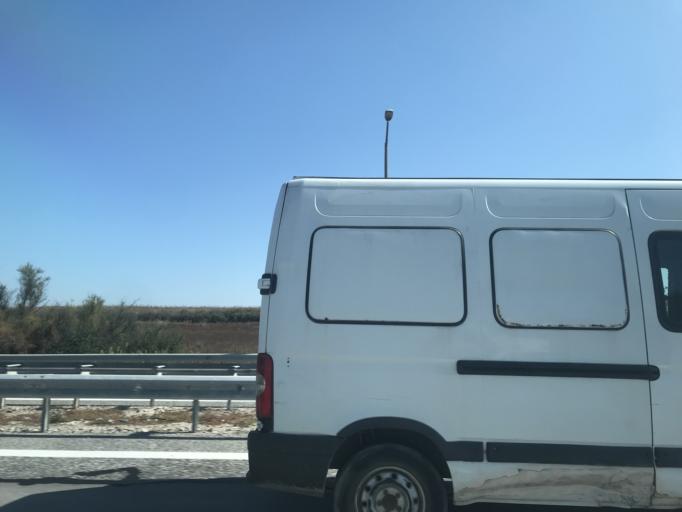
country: TR
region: Kirklareli
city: Luleburgaz
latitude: 41.4472
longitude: 27.3894
